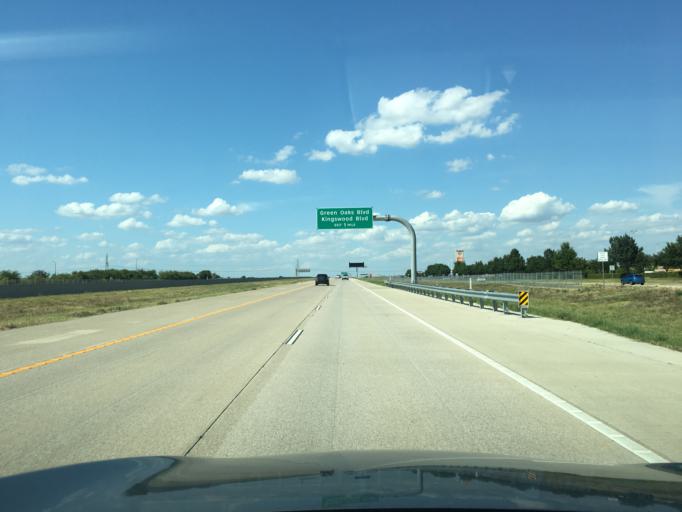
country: US
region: Texas
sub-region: Tarrant County
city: Arlington
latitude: 32.6406
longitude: -97.0632
